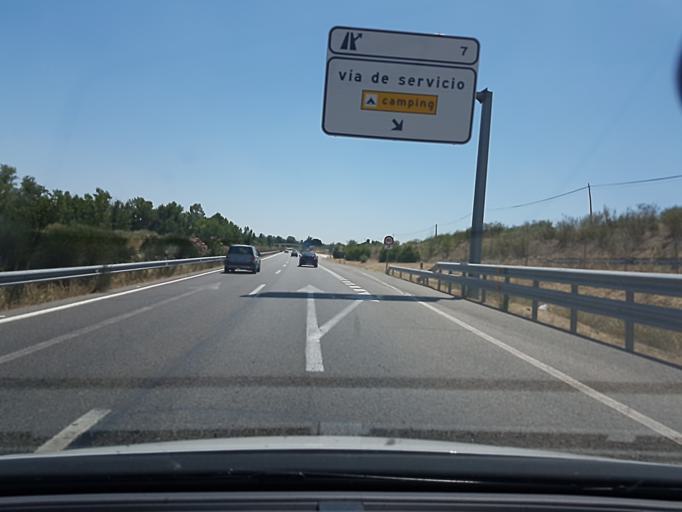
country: ES
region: Madrid
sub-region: Provincia de Madrid
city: Villaviciosa de Odon
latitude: 40.3852
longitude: -3.9041
